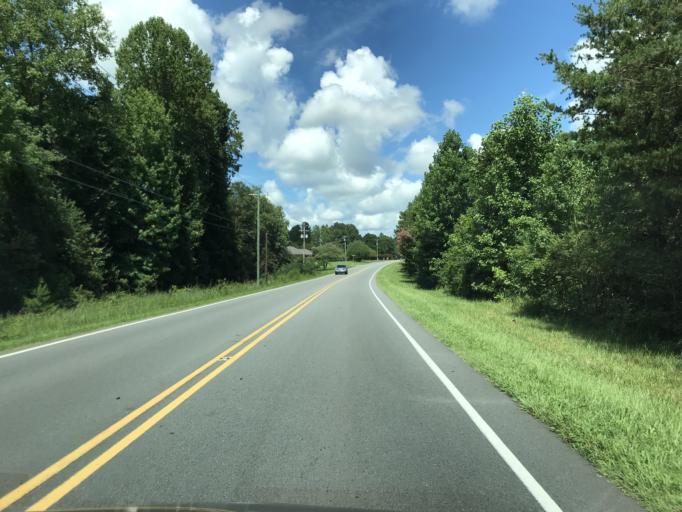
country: US
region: North Carolina
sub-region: Lincoln County
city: Pumpkin Center
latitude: 35.5159
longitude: -81.1525
